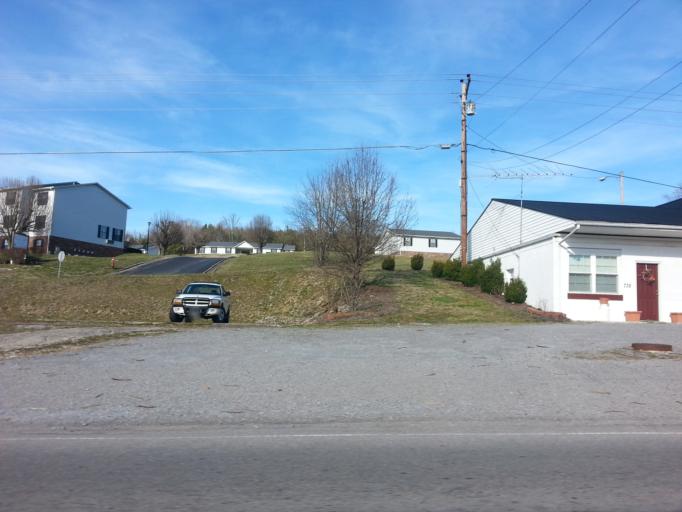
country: US
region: Tennessee
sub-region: Cannon County
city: Woodbury
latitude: 35.8248
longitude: -86.0555
